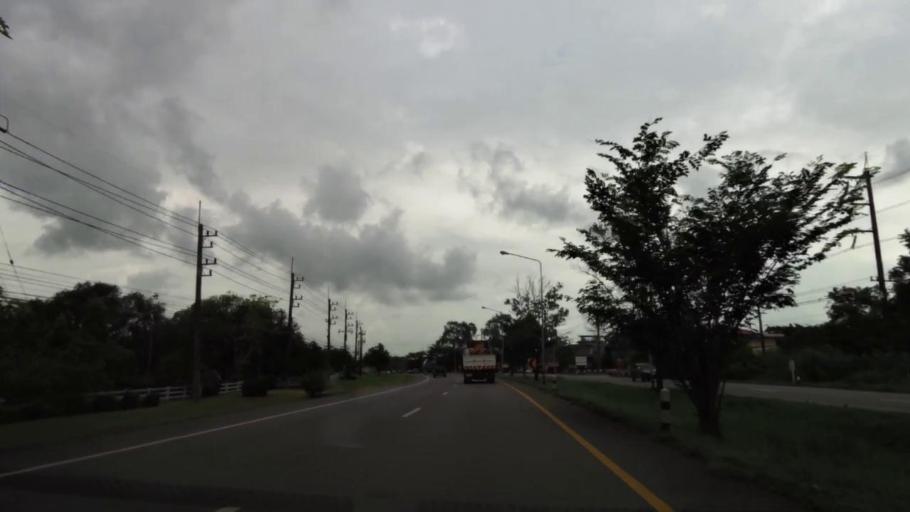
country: TH
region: Chanthaburi
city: Tha Mai
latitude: 12.7136
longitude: 101.9805
